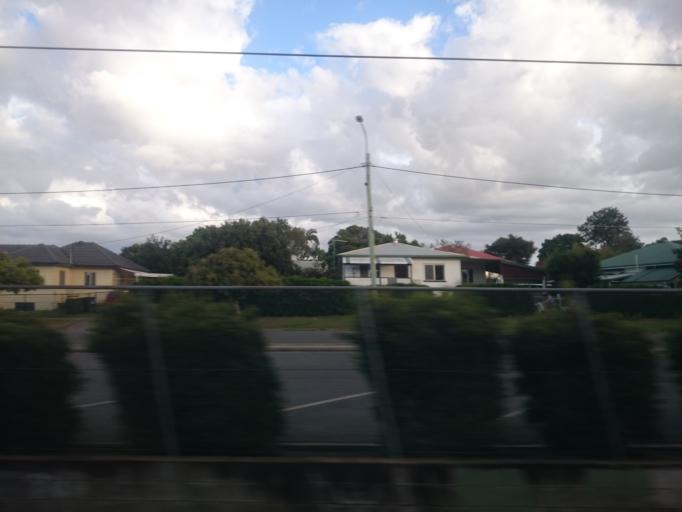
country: AU
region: Queensland
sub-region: Brisbane
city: Wynnum
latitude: -27.4374
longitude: 153.1601
